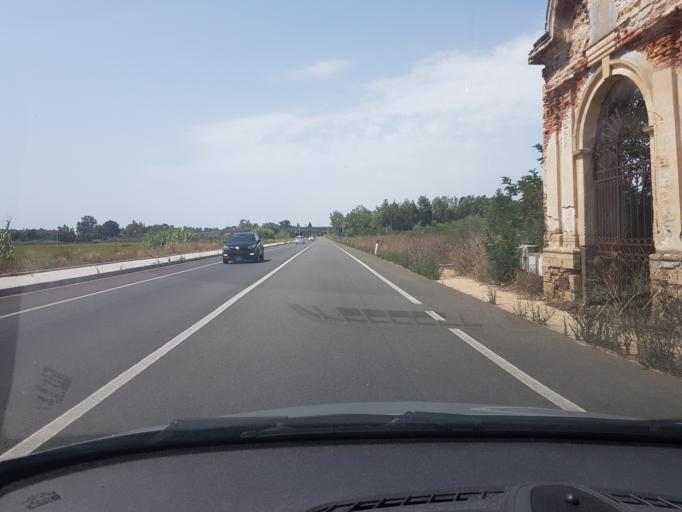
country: IT
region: Sardinia
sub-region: Provincia di Oristano
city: Donigala Fenugheddu
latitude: 39.9293
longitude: 8.5834
